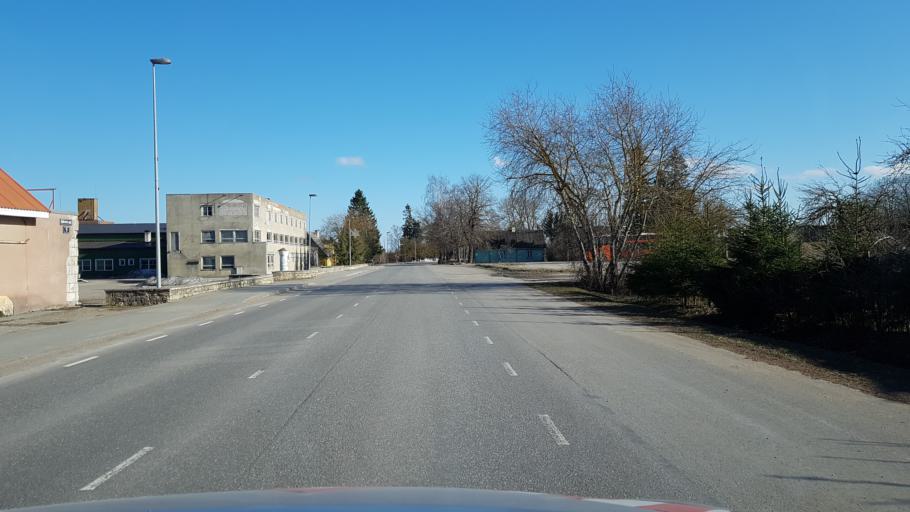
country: EE
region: Laeaene-Virumaa
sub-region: Haljala vald
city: Haljala
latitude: 59.4295
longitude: 26.2668
